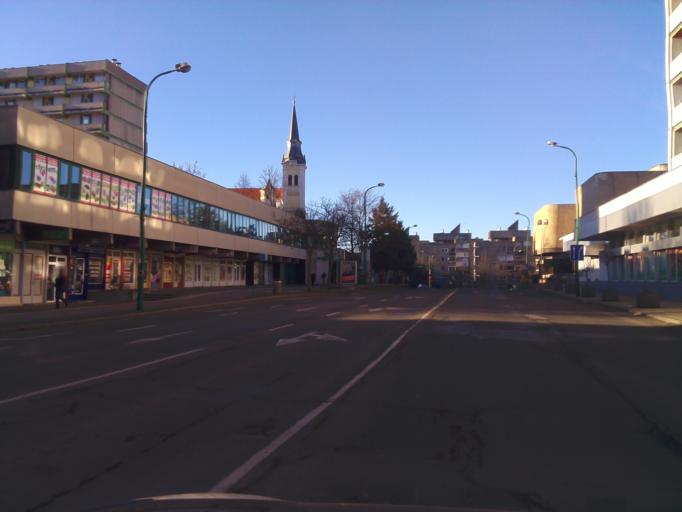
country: HU
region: Nograd
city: Salgotarjan
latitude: 48.1036
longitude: 19.8066
